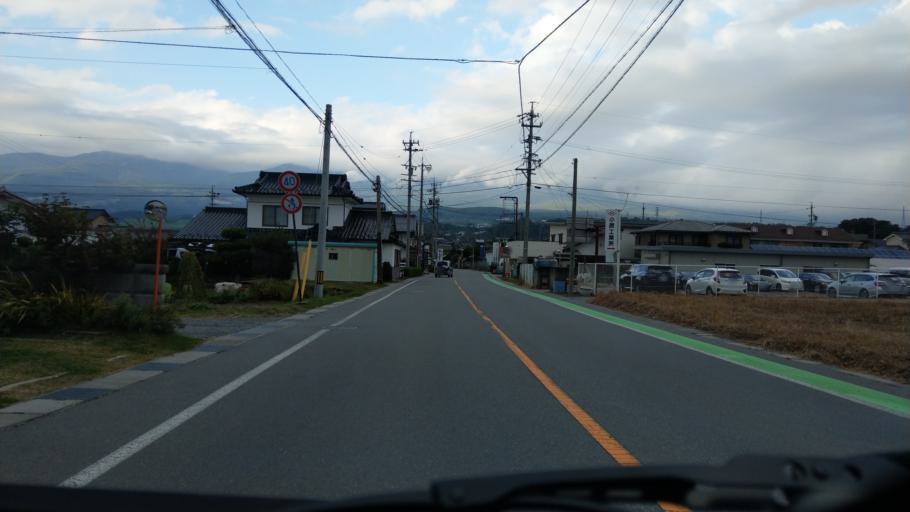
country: JP
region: Nagano
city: Komoro
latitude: 36.3133
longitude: 138.4306
